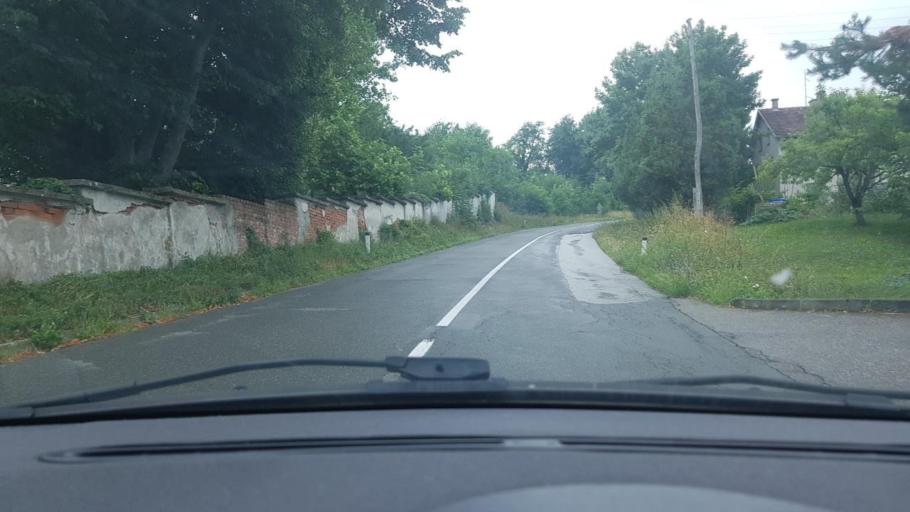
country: AT
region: Styria
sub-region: Politischer Bezirk Suedoststeiermark
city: Mureck
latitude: 46.7051
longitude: 15.7861
